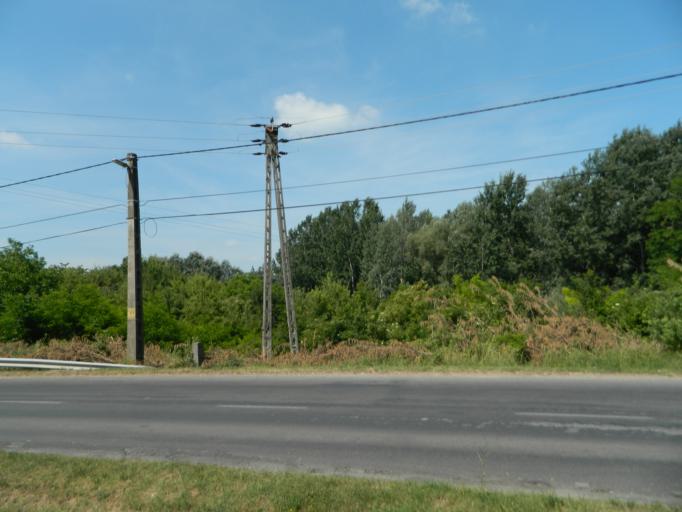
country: HU
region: Somogy
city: Balatonfoldvar
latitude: 46.8516
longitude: 17.8977
